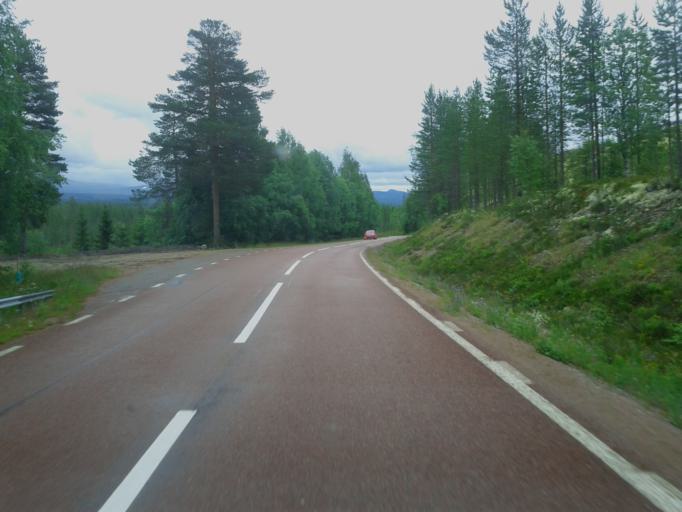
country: NO
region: Hedmark
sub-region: Trysil
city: Innbygda
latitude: 61.8524
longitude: 12.6410
